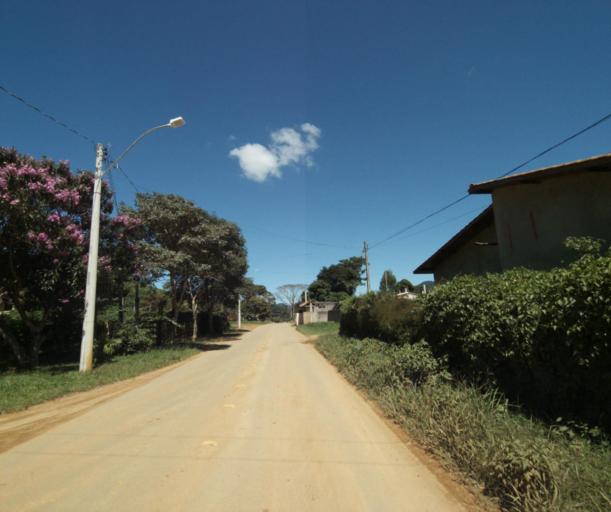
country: BR
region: Minas Gerais
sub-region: Espera Feliz
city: Espera Feliz
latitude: -20.5581
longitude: -41.8208
